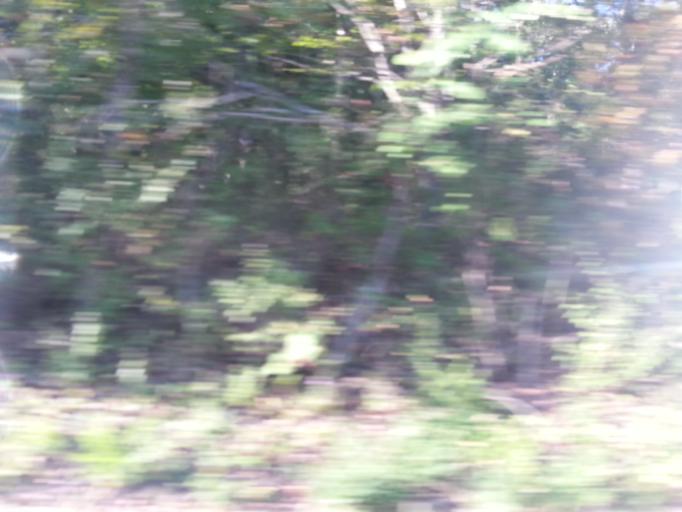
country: US
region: Tennessee
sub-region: Blount County
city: Eagleton Village
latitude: 35.7990
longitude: -83.9226
